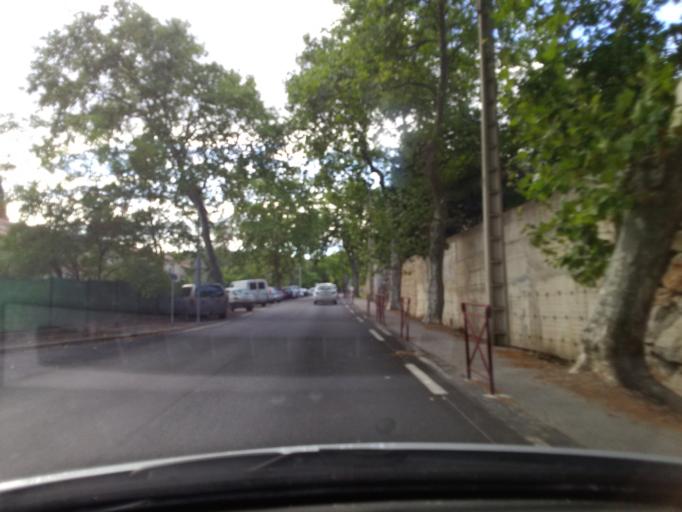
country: FR
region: Languedoc-Roussillon
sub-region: Departement de l'Herault
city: Nebian
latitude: 43.6275
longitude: 3.4217
